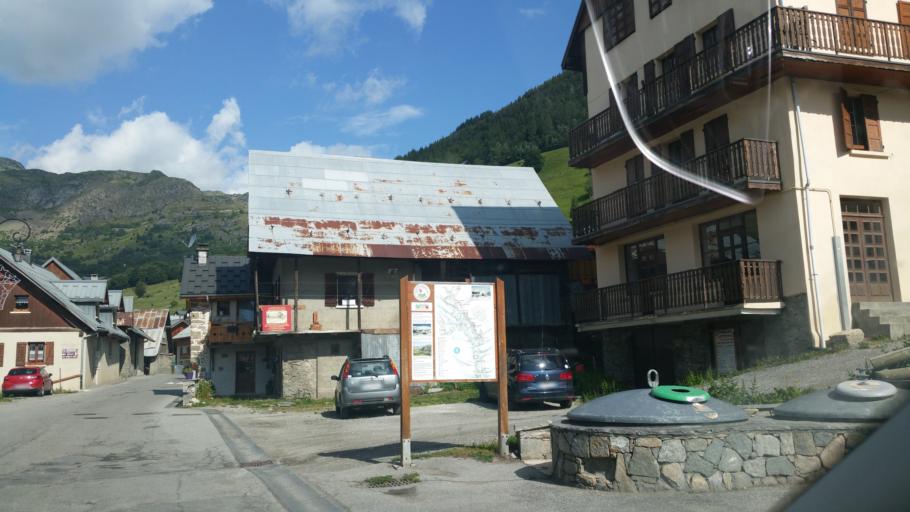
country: FR
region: Rhone-Alpes
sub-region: Departement de la Savoie
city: Saint-Jean-de-Maurienne
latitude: 45.2212
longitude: 6.2341
